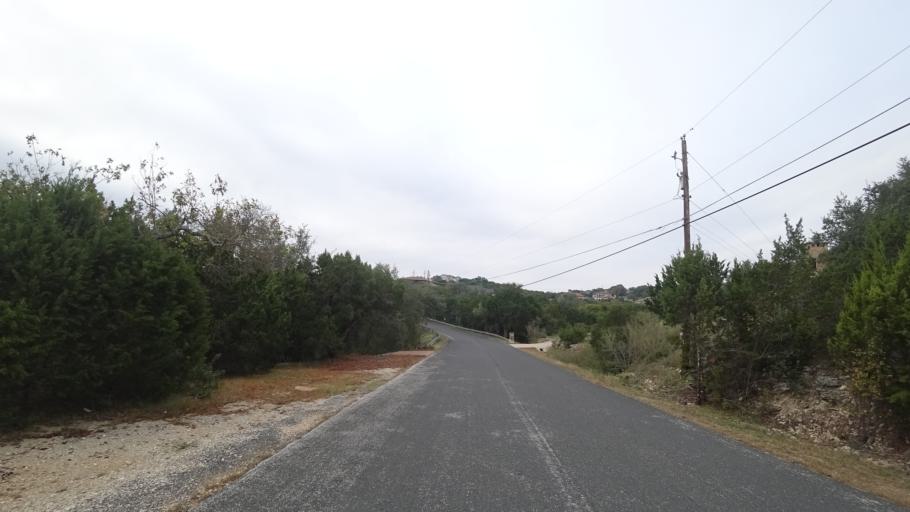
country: US
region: Texas
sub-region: Travis County
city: Hudson Bend
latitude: 30.3939
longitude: -97.9148
